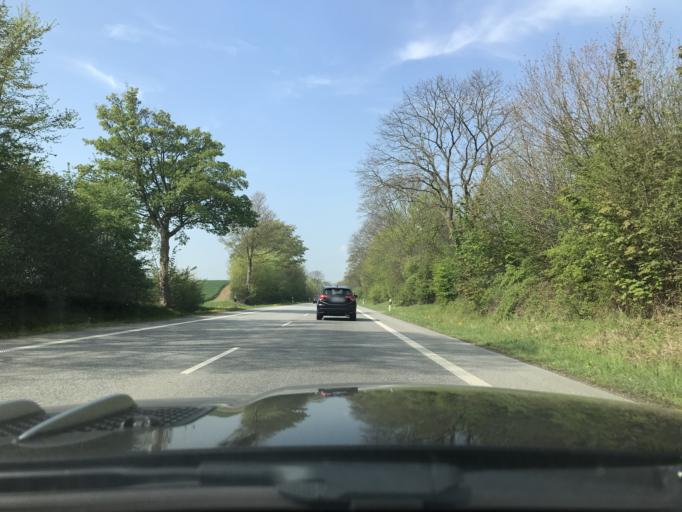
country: DE
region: Schleswig-Holstein
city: Gromitz
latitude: 54.1492
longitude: 10.9425
